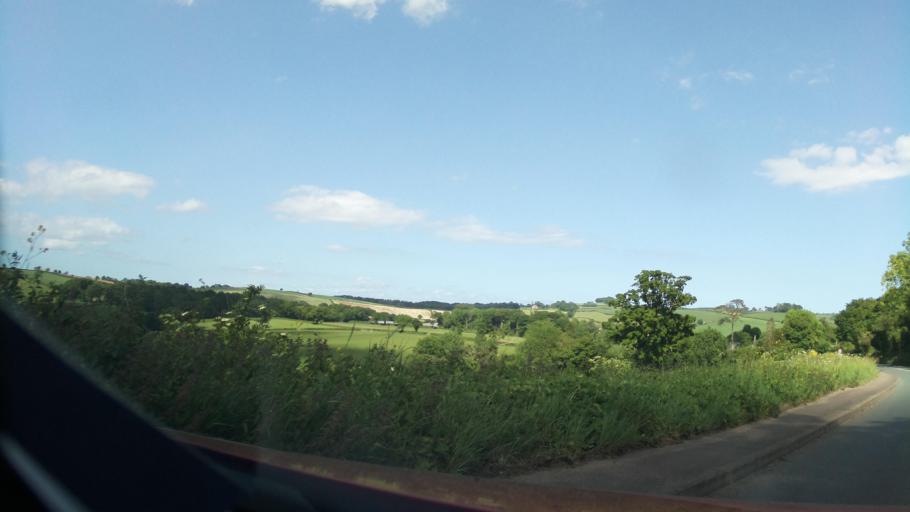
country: GB
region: England
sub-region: Devon
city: Totnes
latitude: 50.4322
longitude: -3.6665
